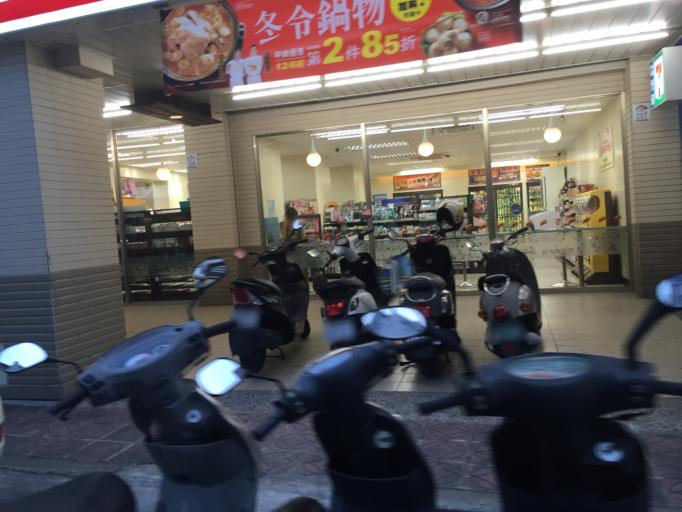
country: TW
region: Taiwan
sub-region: Yilan
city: Yilan
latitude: 24.7608
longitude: 121.7534
